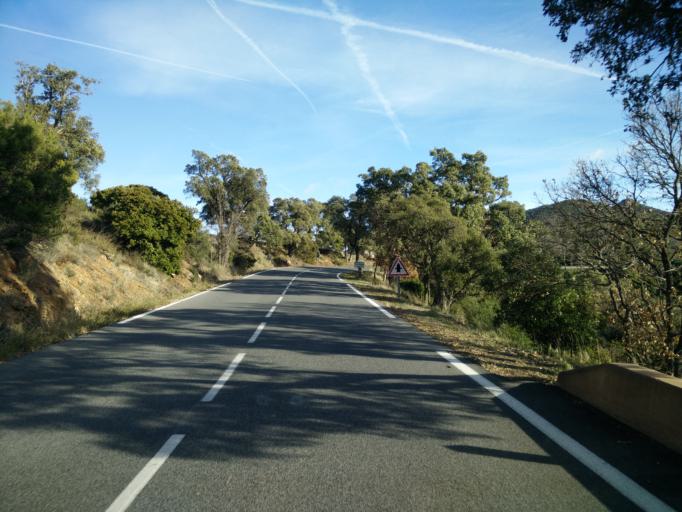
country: FR
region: Provence-Alpes-Cote d'Azur
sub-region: Departement du Var
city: Saint-Raphael
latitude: 43.5013
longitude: 6.7928
